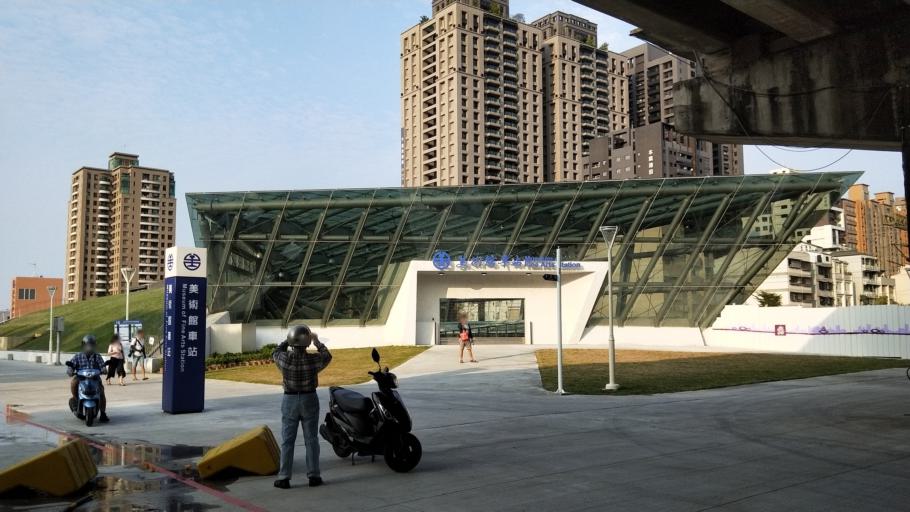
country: TW
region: Kaohsiung
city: Kaohsiung
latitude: 22.6517
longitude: 120.2810
